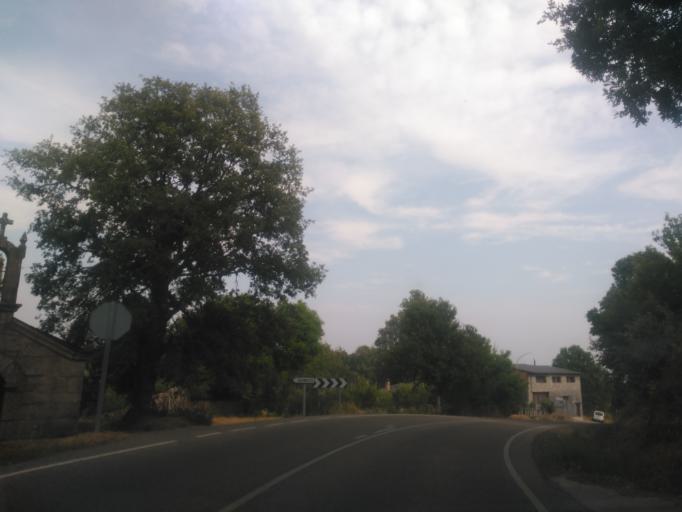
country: ES
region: Castille and Leon
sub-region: Provincia de Zamora
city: Galende
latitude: 42.0996
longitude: -6.6517
